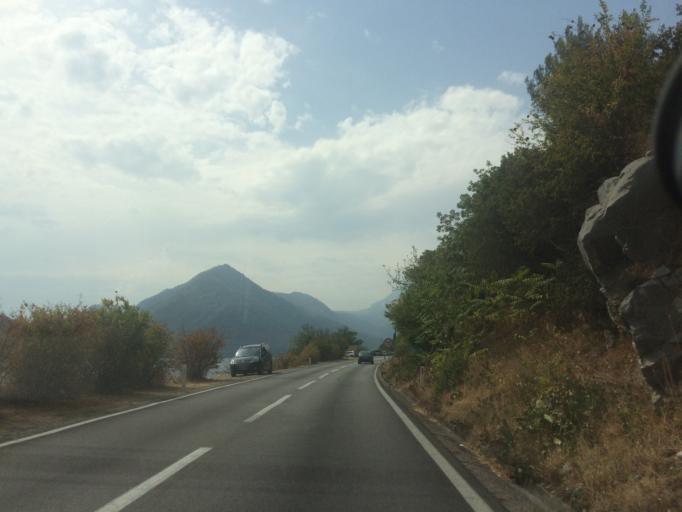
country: ME
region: Kotor
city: Risan
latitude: 42.4839
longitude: 18.7106
